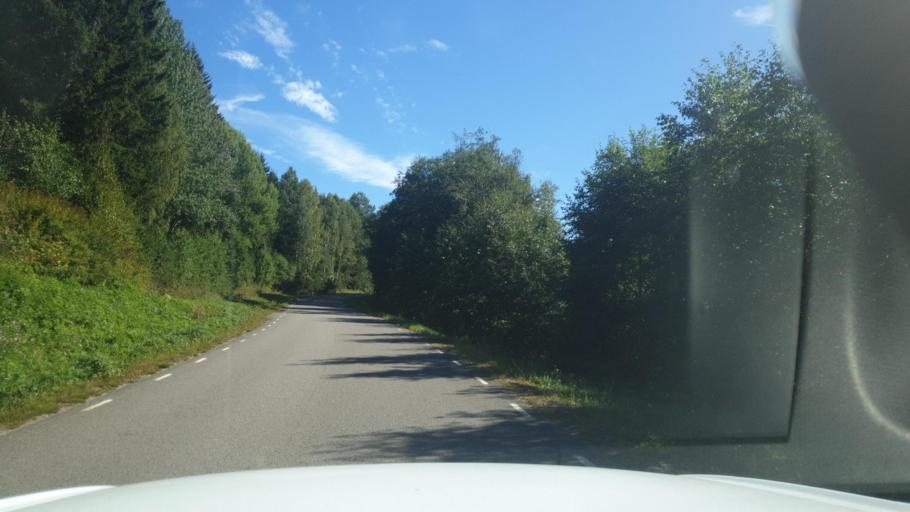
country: SE
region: Vaermland
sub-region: Torsby Kommun
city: Torsby
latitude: 60.0148
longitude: 12.6616
